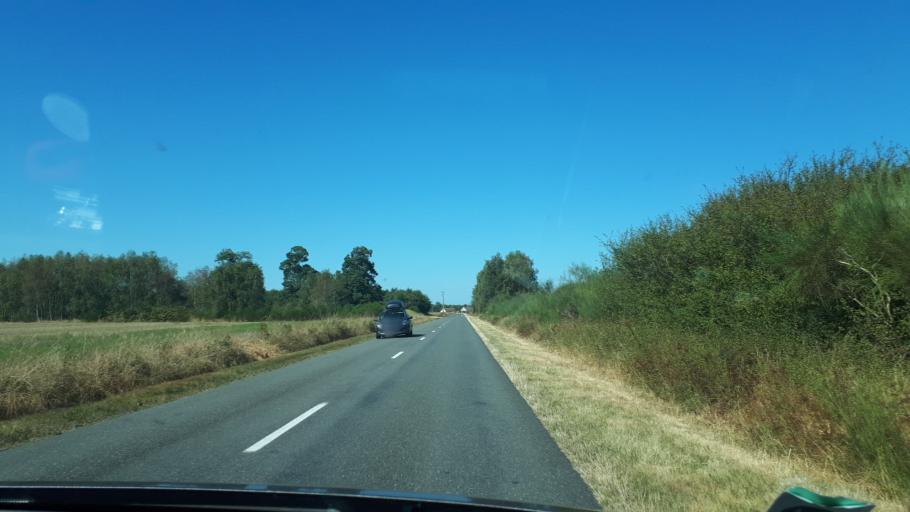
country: FR
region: Centre
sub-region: Departement du Loiret
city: Coullons
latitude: 47.6371
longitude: 2.4318
